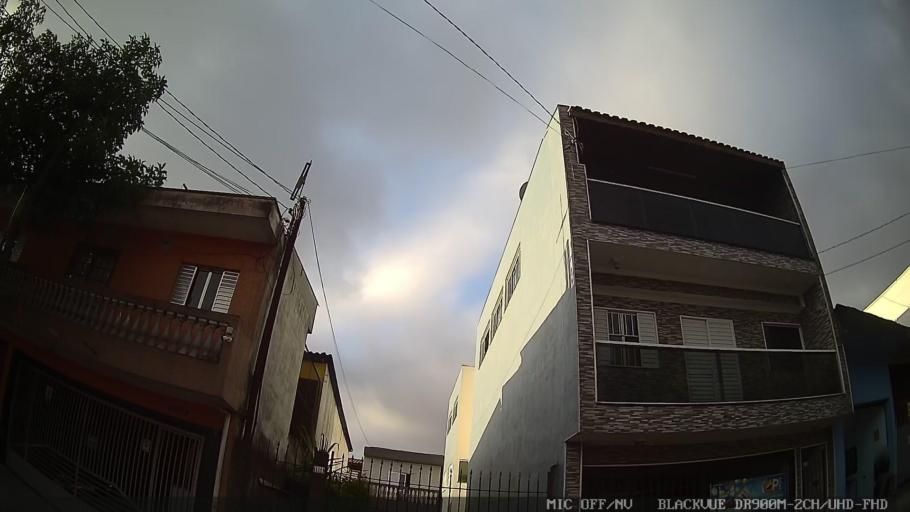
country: BR
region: Sao Paulo
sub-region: Sao Caetano Do Sul
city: Sao Caetano do Sul
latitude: -23.5704
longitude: -46.4905
